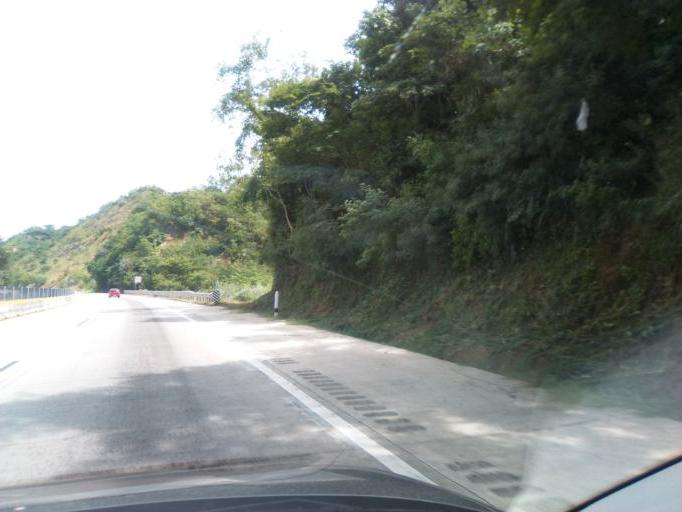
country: MX
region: Guerrero
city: Tierra Colorada
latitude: 17.1875
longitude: -99.5440
